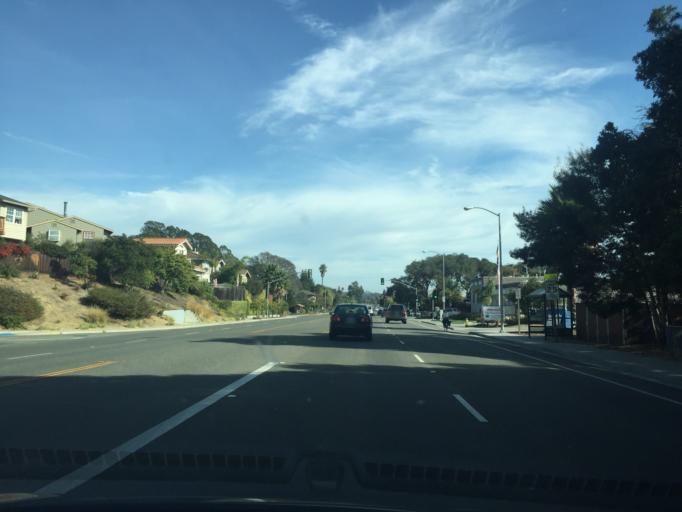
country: US
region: California
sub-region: Santa Cruz County
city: Seacliff
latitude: 36.9866
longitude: -121.9197
